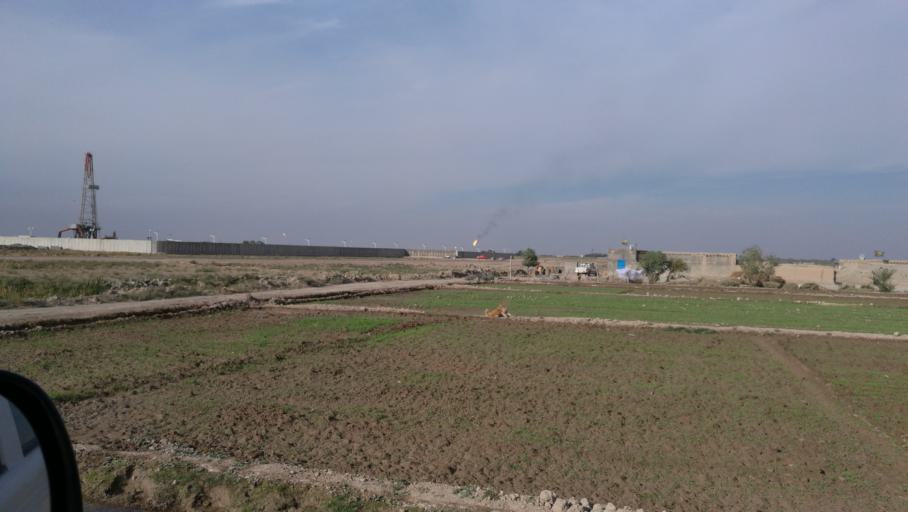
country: IQ
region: Dhi Qar
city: Ar Rifa`i
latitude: 31.7342
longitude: 46.0637
